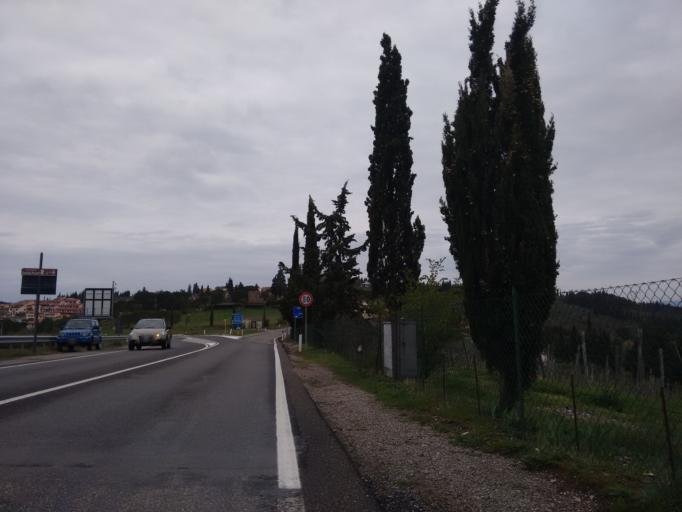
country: IT
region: Tuscany
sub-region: Province of Florence
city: Strada in Chianti
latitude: 43.6514
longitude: 11.3091
